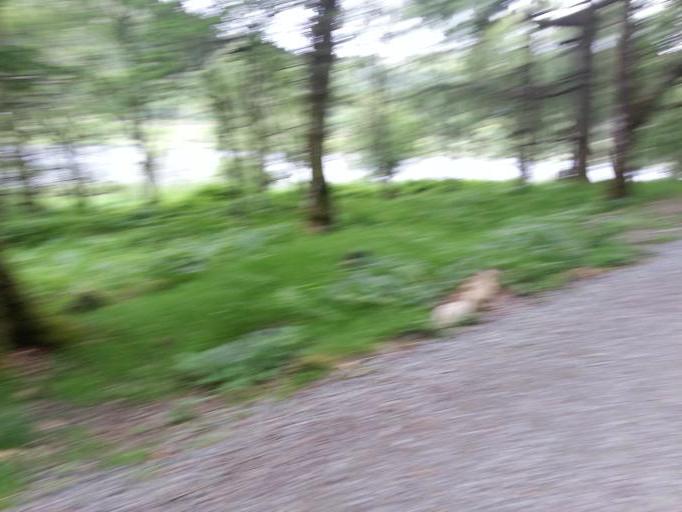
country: IE
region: Leinster
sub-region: Wicklow
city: Rathdrum
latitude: 53.0074
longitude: -6.3365
